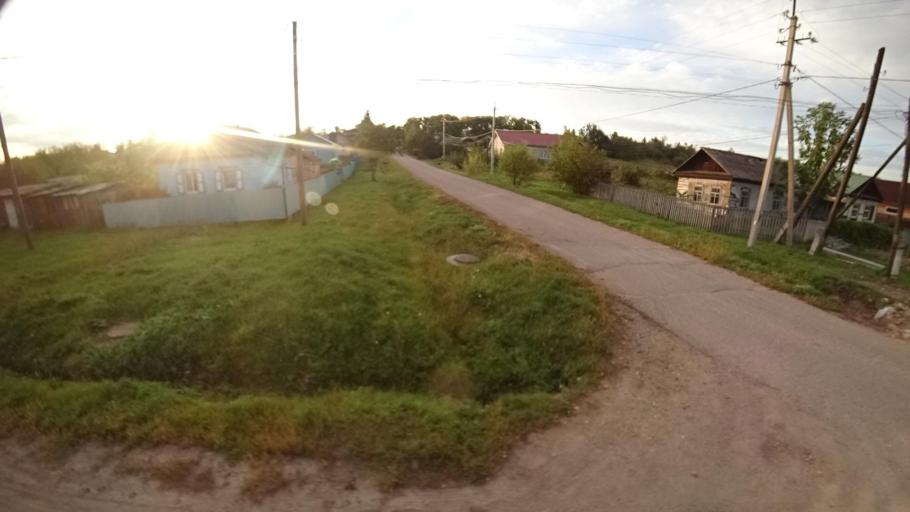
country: RU
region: Primorskiy
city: Yakovlevka
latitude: 44.4234
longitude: 133.4795
